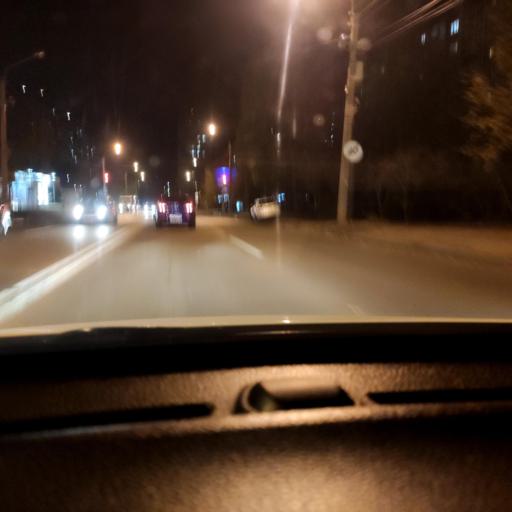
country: RU
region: Voronezj
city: Podgornoye
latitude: 51.7167
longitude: 39.1643
